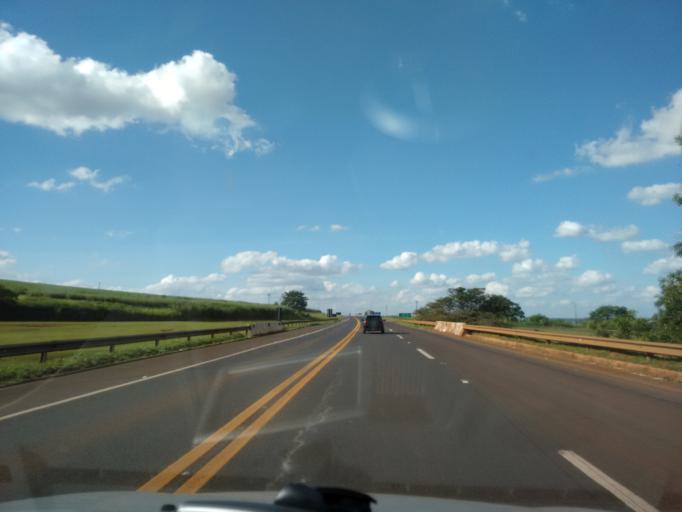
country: BR
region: Sao Paulo
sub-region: Americo Brasiliense
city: Americo Brasiliense
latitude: -21.7551
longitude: -48.0694
